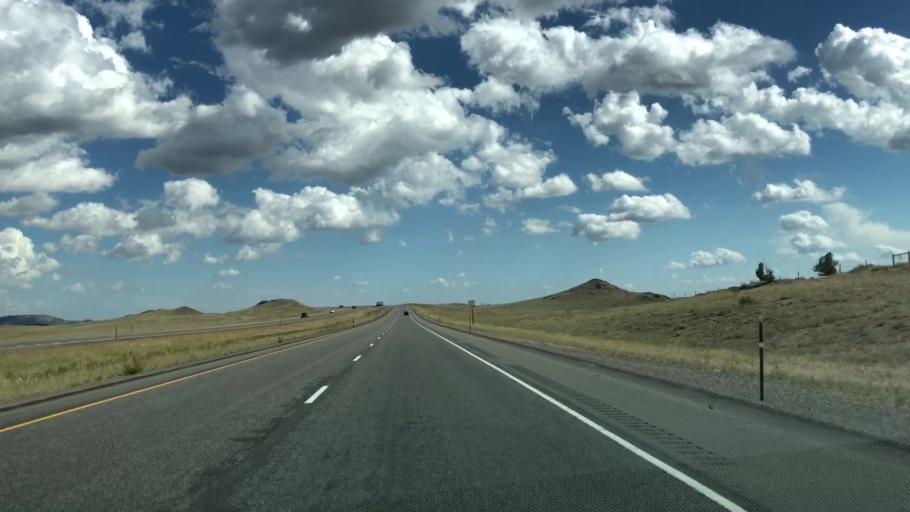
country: US
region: Wyoming
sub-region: Albany County
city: Laramie
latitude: 41.0489
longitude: -105.4669
